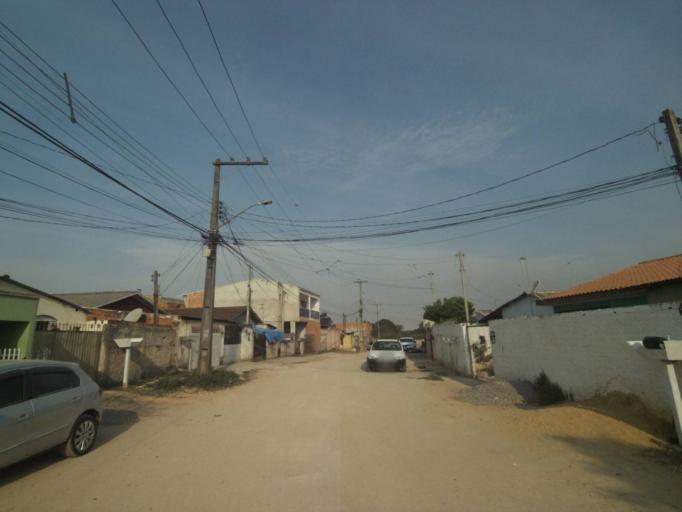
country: BR
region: Parana
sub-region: Sao Jose Dos Pinhais
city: Sao Jose dos Pinhais
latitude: -25.4984
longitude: -49.2078
